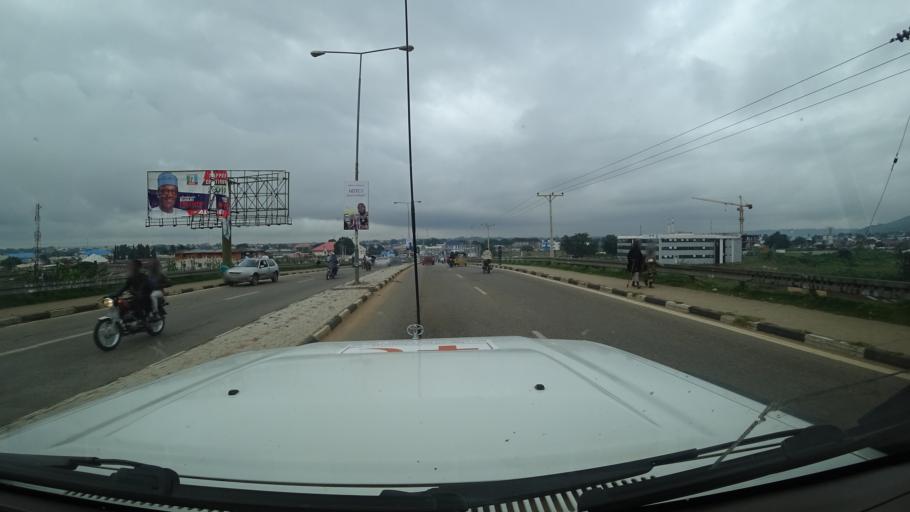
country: NG
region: Niger
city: Minna
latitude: 9.6131
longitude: 6.5490
